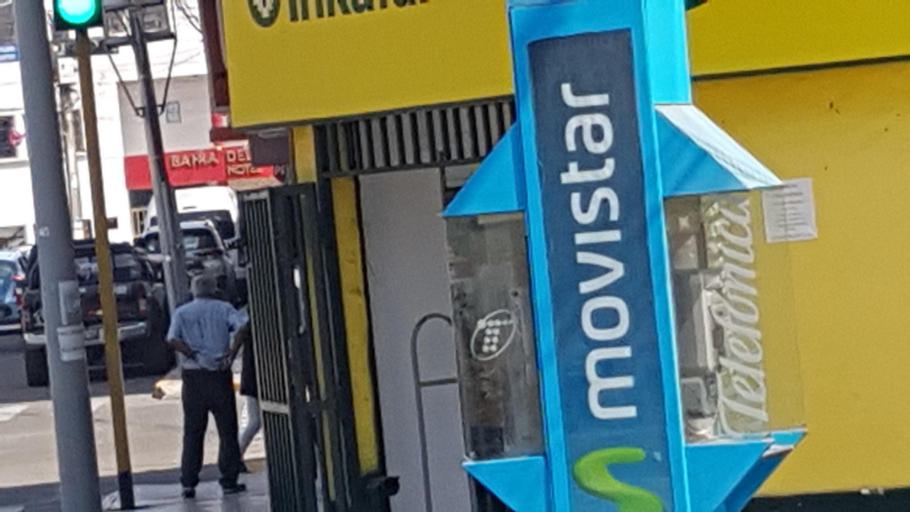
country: PE
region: Arequipa
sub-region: Provincia de Islay
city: Mollendo
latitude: -17.0289
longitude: -72.0157
